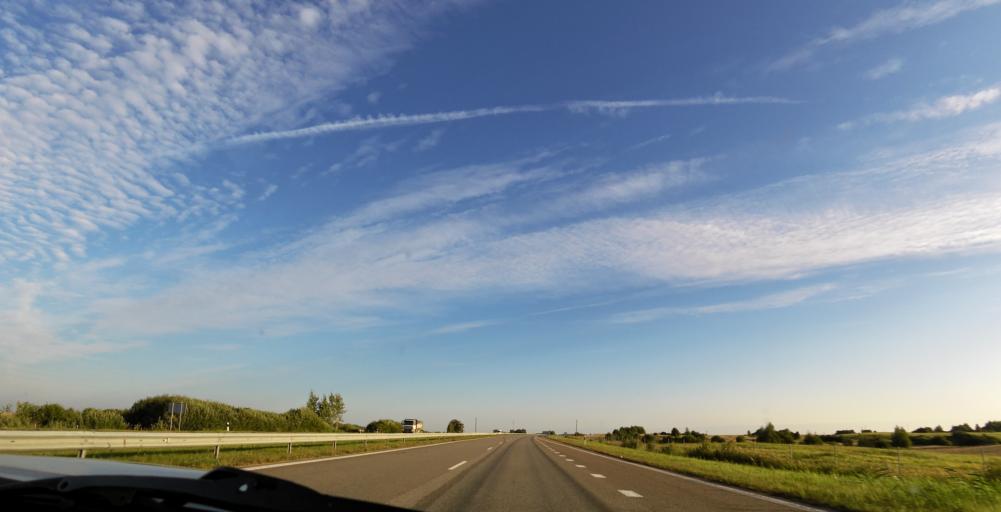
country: LT
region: Vilnius County
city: Ukmerge
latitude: 55.1827
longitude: 24.8111
